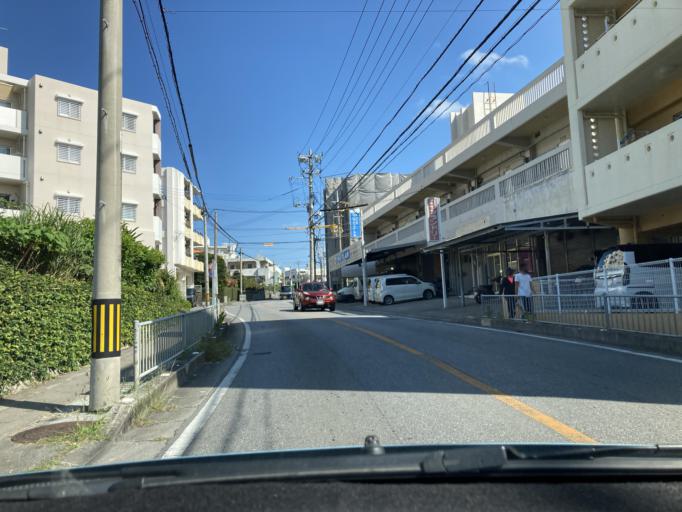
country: JP
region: Okinawa
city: Tomigusuku
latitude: 26.1825
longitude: 127.6652
